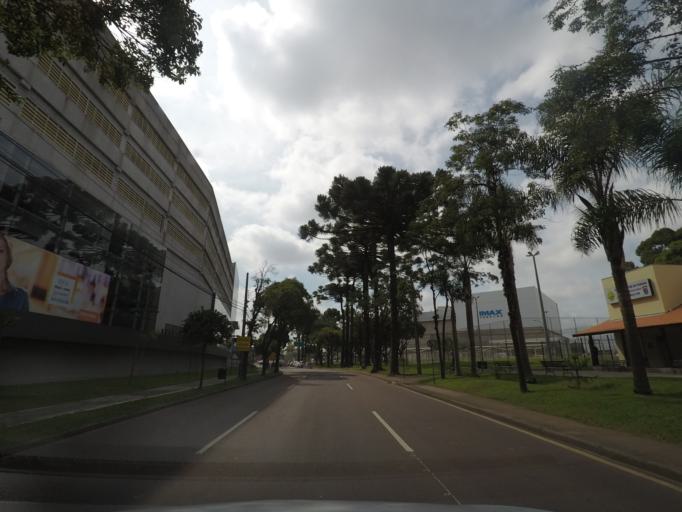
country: BR
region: Parana
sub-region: Curitiba
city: Curitiba
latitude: -25.4789
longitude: -49.2936
